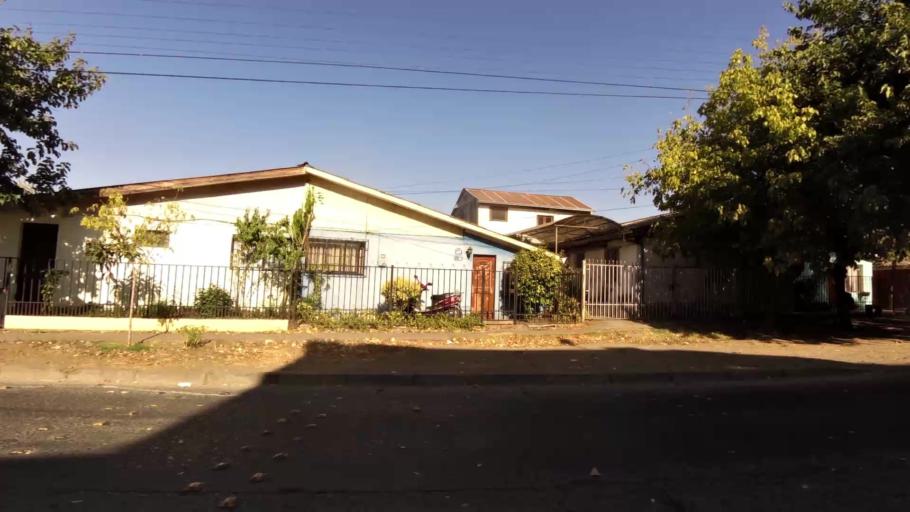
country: CL
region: Maule
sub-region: Provincia de Talca
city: Talca
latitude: -35.4376
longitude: -71.6704
